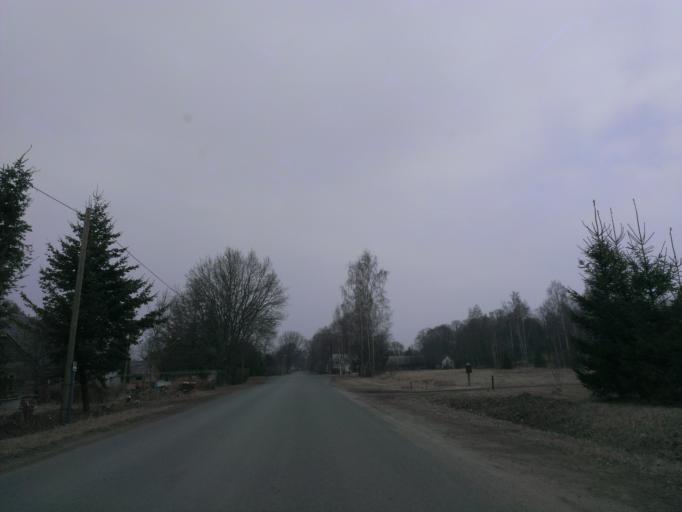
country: LV
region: Salacgrivas
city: Ainazi
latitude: 58.0013
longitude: 24.4370
